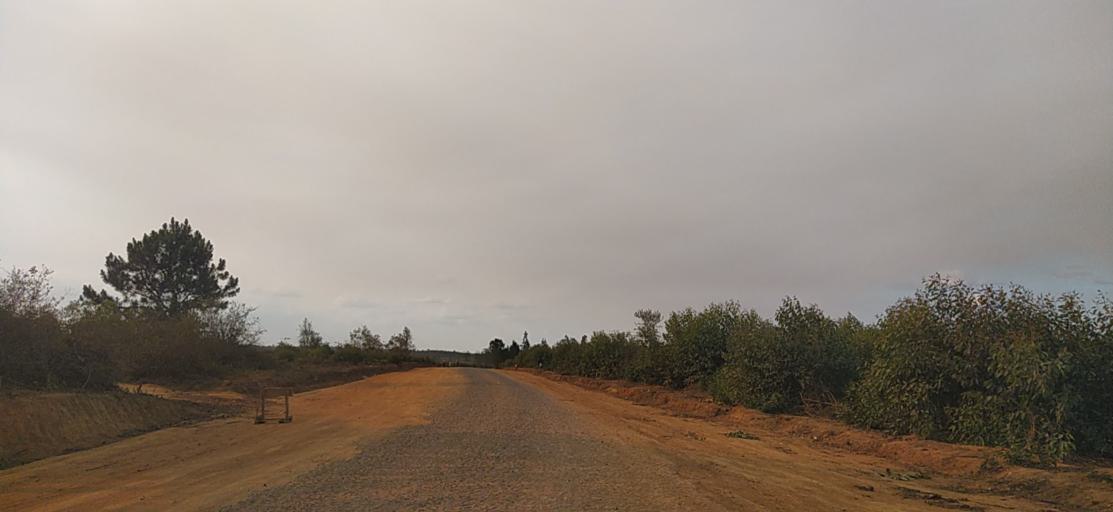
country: MG
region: Alaotra Mangoro
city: Moramanga
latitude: -18.5999
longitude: 48.2787
